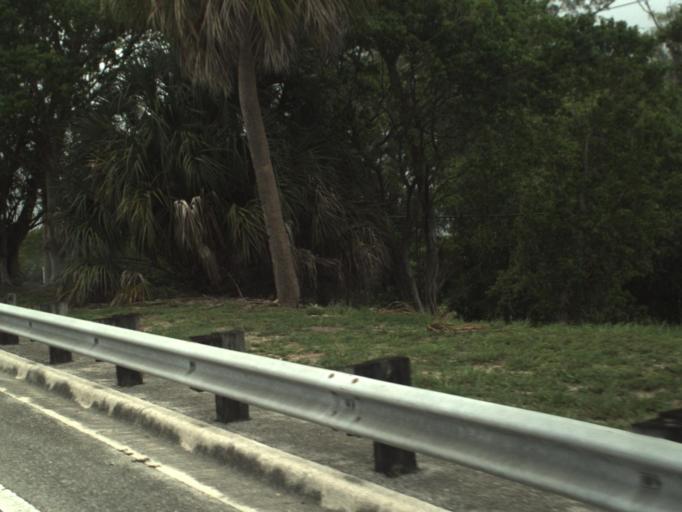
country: US
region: Florida
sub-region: Palm Beach County
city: Boca Pointe
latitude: 26.3504
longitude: -80.1694
